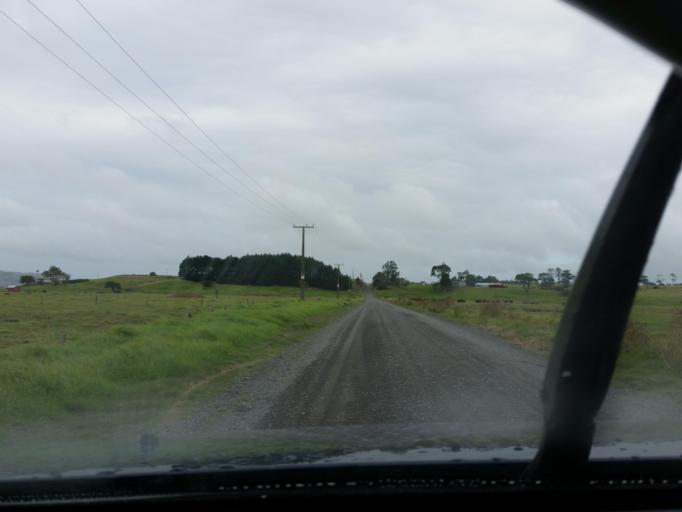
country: NZ
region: Northland
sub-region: Kaipara District
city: Dargaville
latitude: -36.0088
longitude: 173.8881
